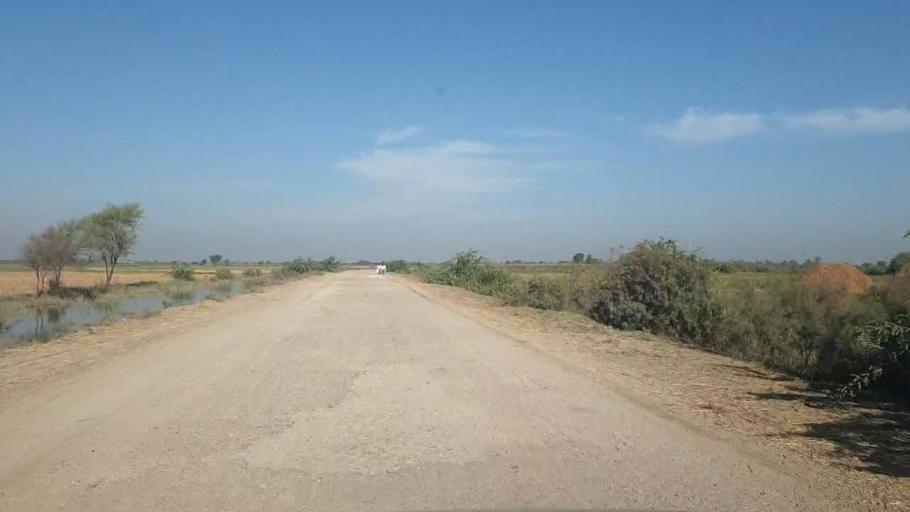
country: PK
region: Sindh
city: Talhar
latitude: 24.9154
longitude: 68.8042
